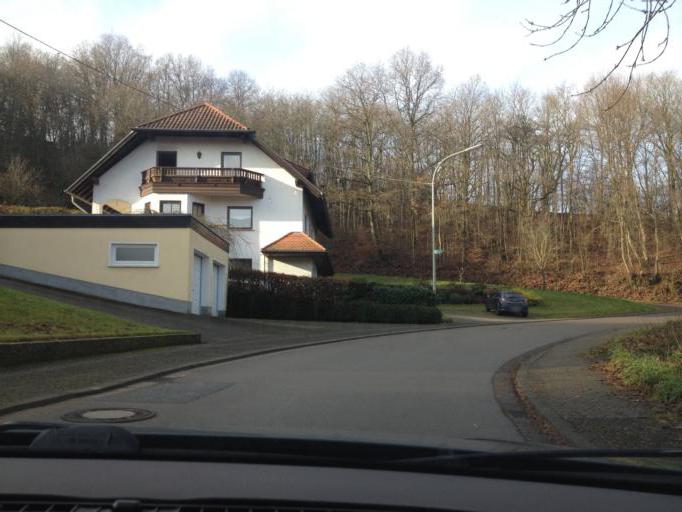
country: DE
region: Saarland
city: Marpingen
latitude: 49.4532
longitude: 7.0502
